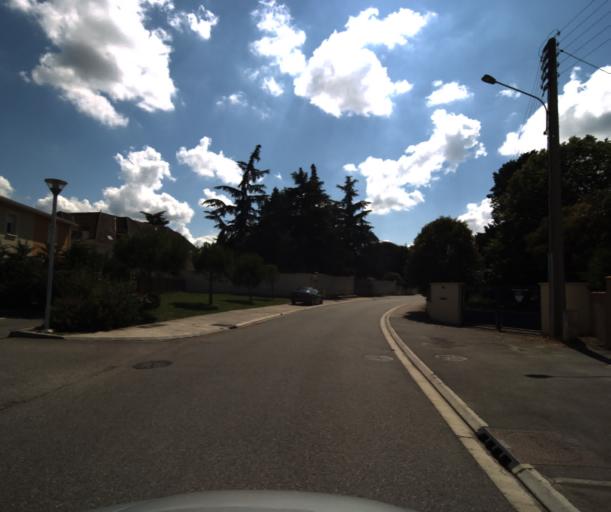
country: FR
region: Midi-Pyrenees
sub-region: Departement de la Haute-Garonne
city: Lacroix-Falgarde
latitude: 43.4810
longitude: 1.3955
